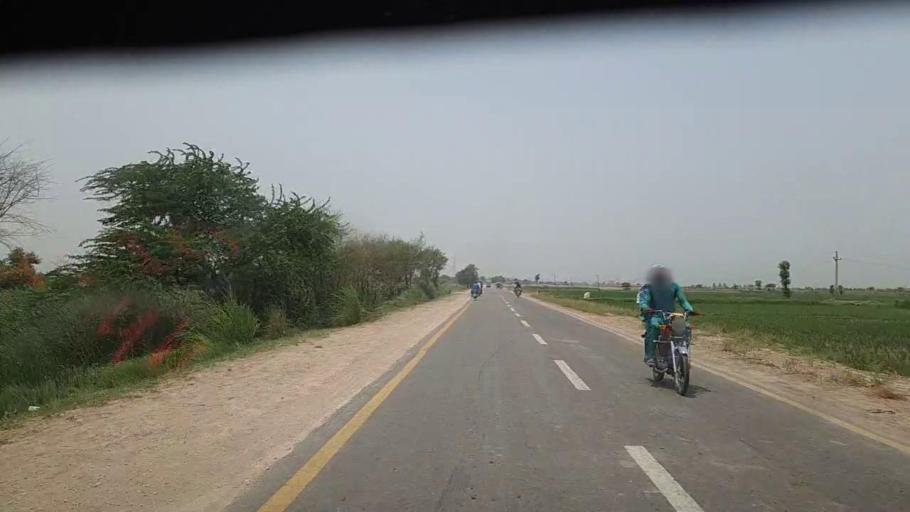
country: PK
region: Sindh
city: Sita Road
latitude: 27.0410
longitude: 67.8645
